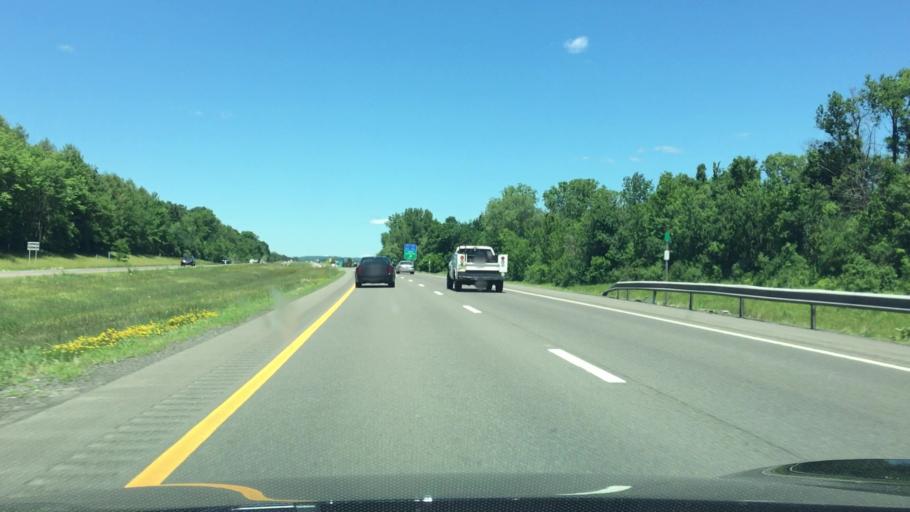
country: US
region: New York
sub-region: Cortland County
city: Homer
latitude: 42.7070
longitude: -76.1491
